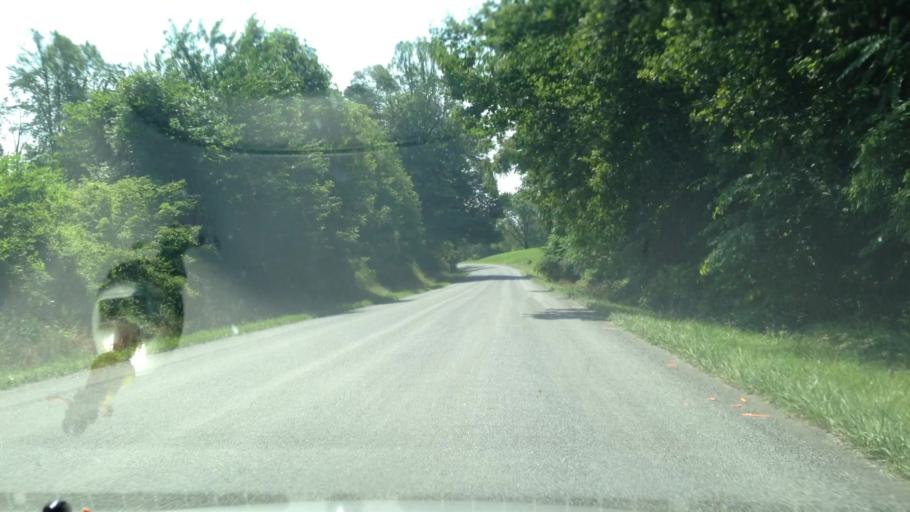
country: US
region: Virginia
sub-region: Patrick County
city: Stuart
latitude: 36.5956
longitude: -80.2945
